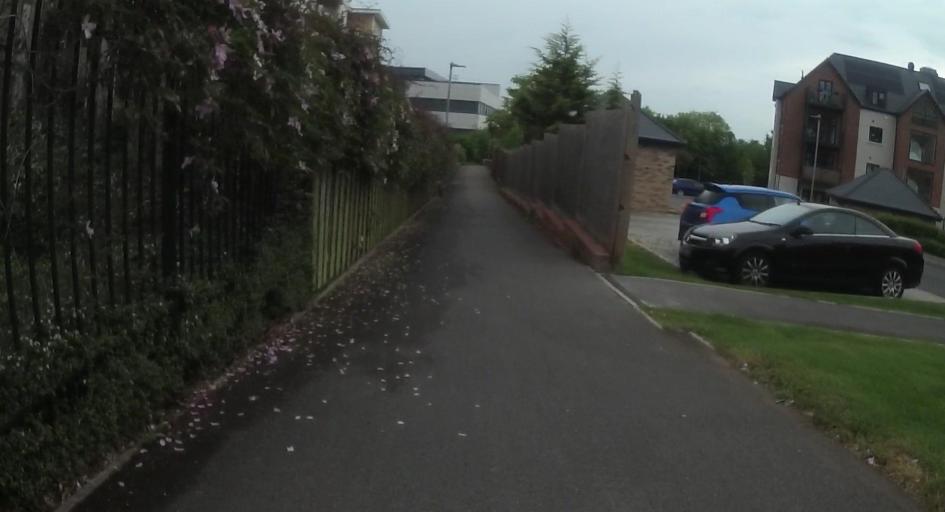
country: GB
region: England
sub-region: Bracknell Forest
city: Bracknell
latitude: 51.4214
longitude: -0.7488
